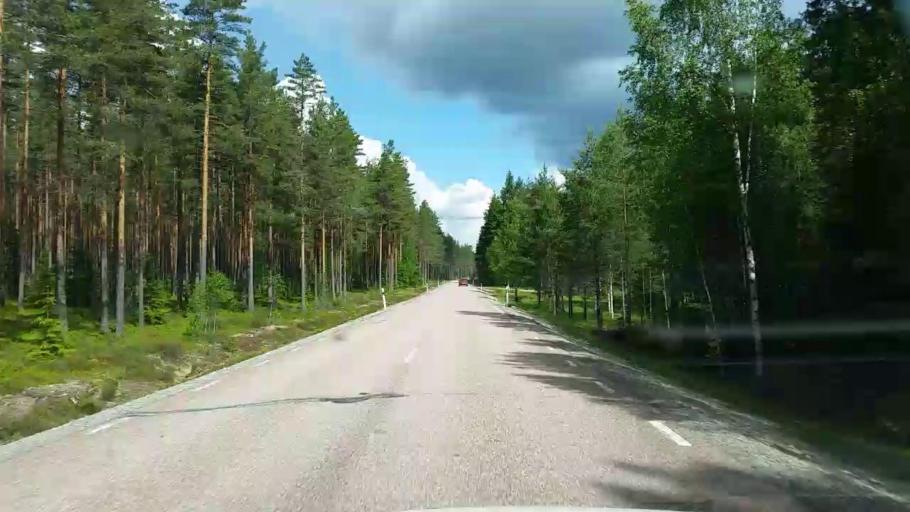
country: SE
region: Vaestmanland
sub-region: Skinnskattebergs Kommun
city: Skinnskatteberg
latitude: 59.8103
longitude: 15.8410
